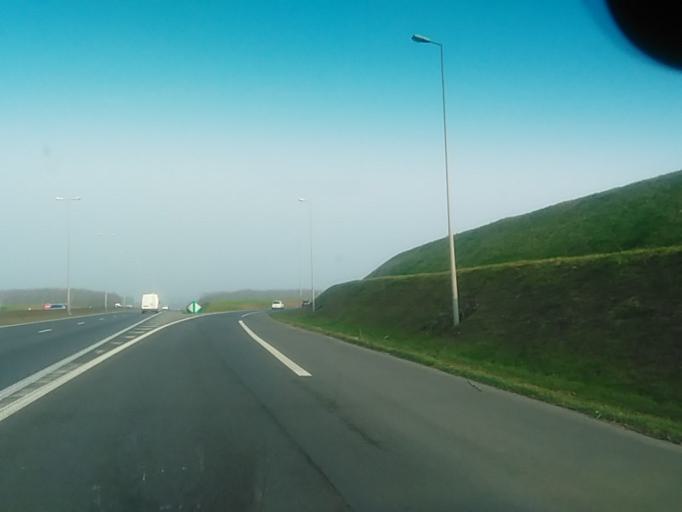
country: FR
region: Lower Normandy
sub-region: Departement du Calvados
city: Eterville
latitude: 49.1494
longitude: -0.4136
